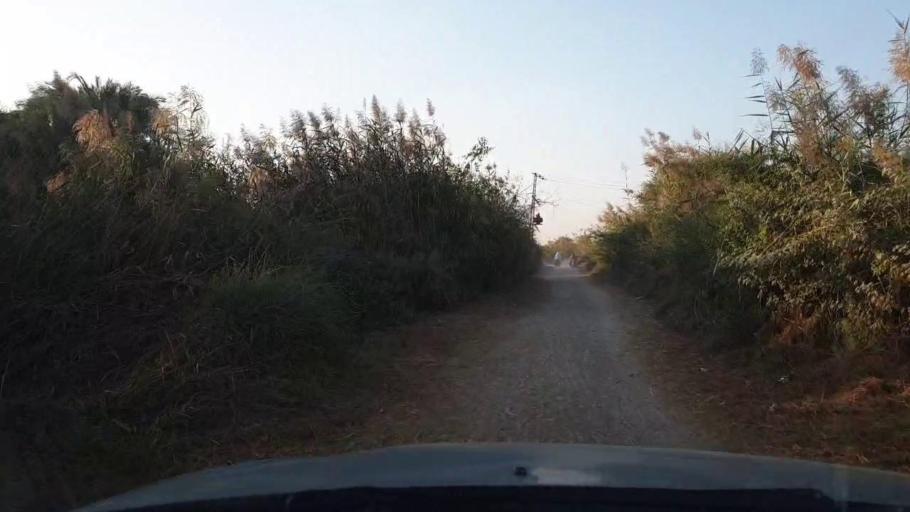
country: PK
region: Sindh
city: Matli
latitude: 25.0354
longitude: 68.6300
